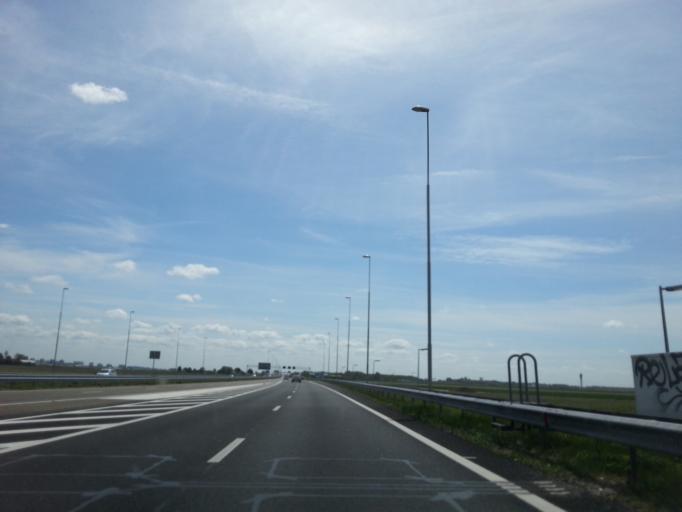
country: NL
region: North Holland
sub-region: Gemeente Haarlemmermeer
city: Hoofddorp
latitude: 52.3496
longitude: 4.7358
